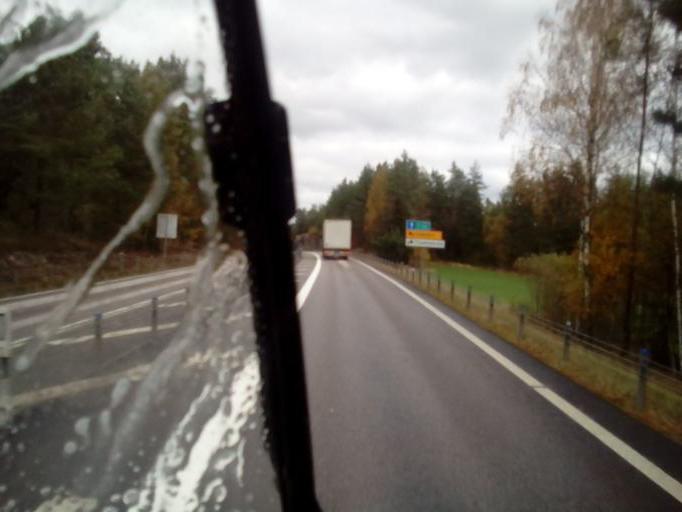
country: SE
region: OEstergoetland
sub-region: Valdemarsviks Kommun
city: Valdemarsvik
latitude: 58.1361
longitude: 16.5341
